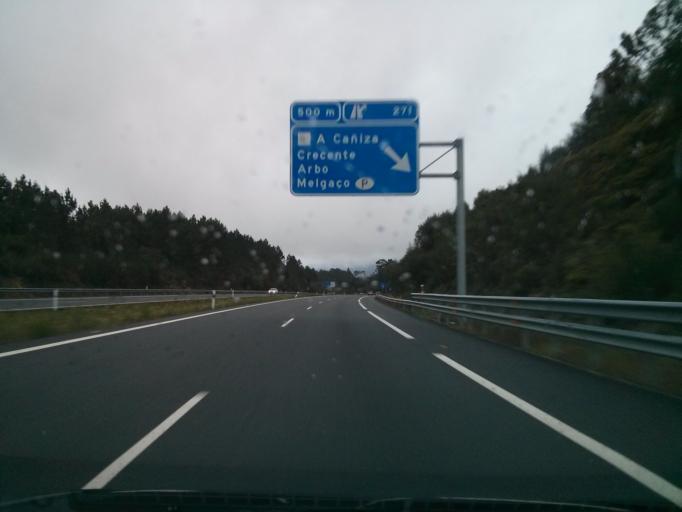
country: ES
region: Galicia
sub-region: Provincia de Ourense
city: Melon
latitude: 42.2143
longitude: -8.2599
